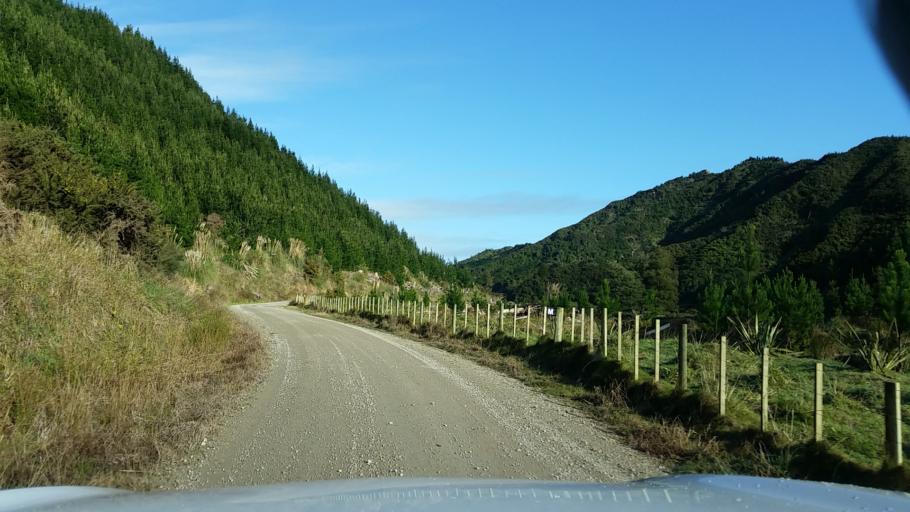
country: NZ
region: Taranaki
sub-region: South Taranaki District
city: Patea
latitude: -39.6923
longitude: 174.7516
